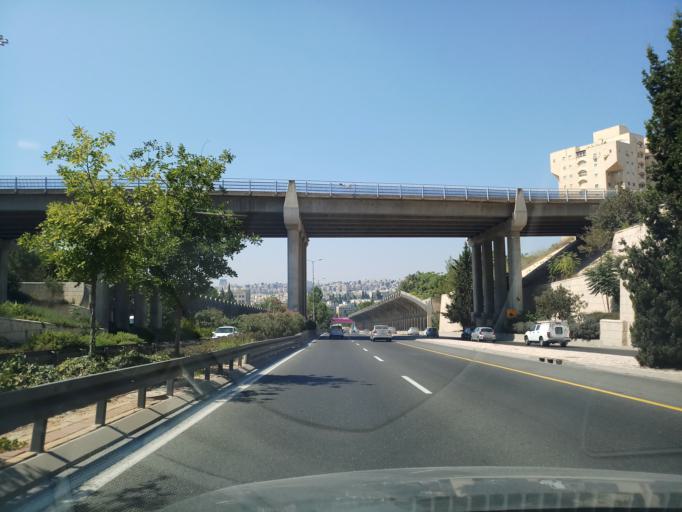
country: IL
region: Jerusalem
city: West Jerusalem
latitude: 31.7828
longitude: 35.1974
